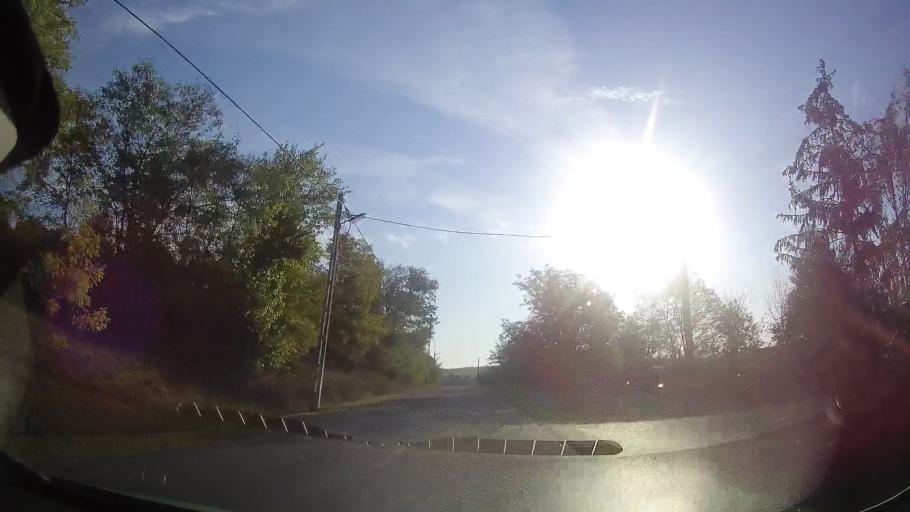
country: RO
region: Timis
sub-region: Comuna Bogda
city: Bogda
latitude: 45.9741
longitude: 21.5959
